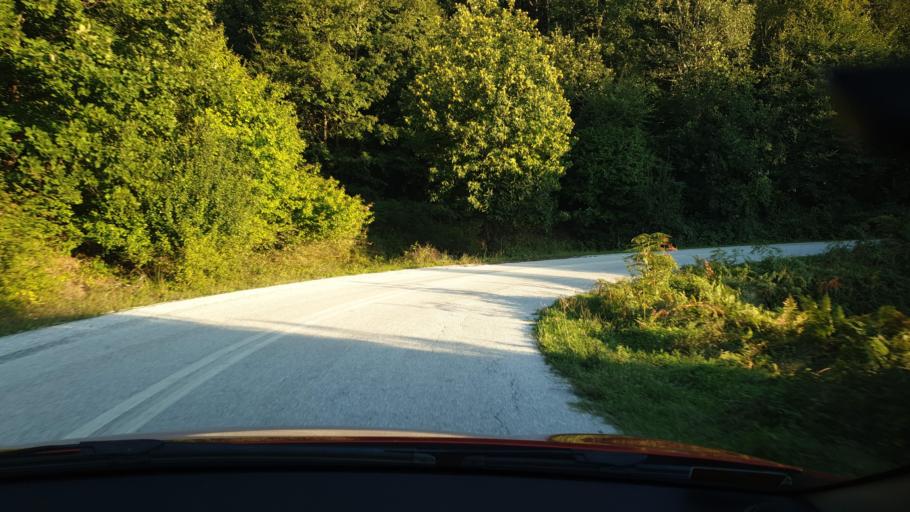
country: GR
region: Central Macedonia
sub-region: Nomos Chalkidikis
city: Galatista
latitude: 40.5065
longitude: 23.2502
